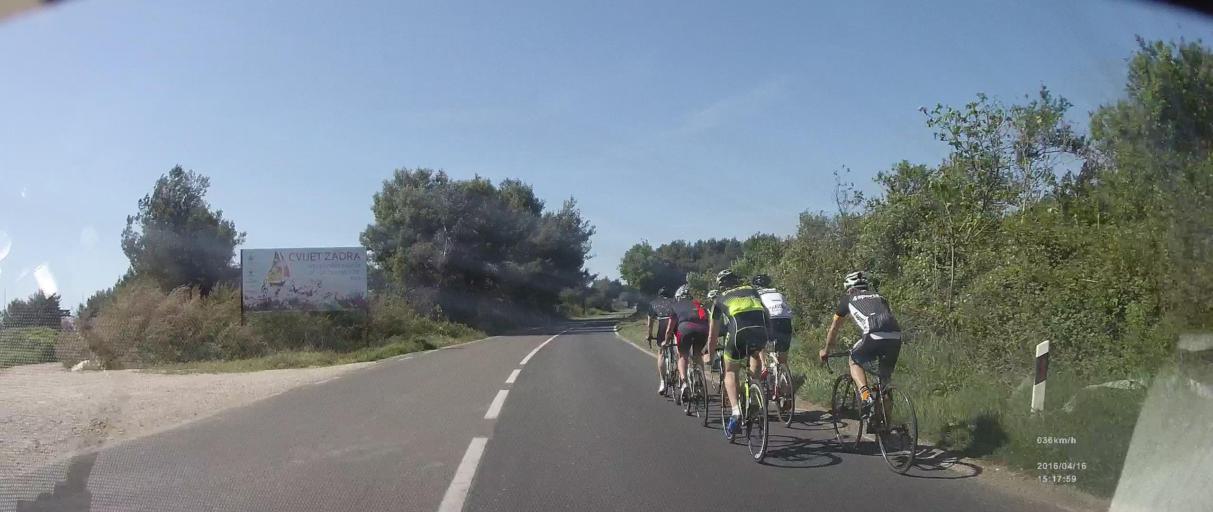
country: HR
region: Zadarska
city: Bibinje
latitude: 44.0574
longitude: 15.3007
